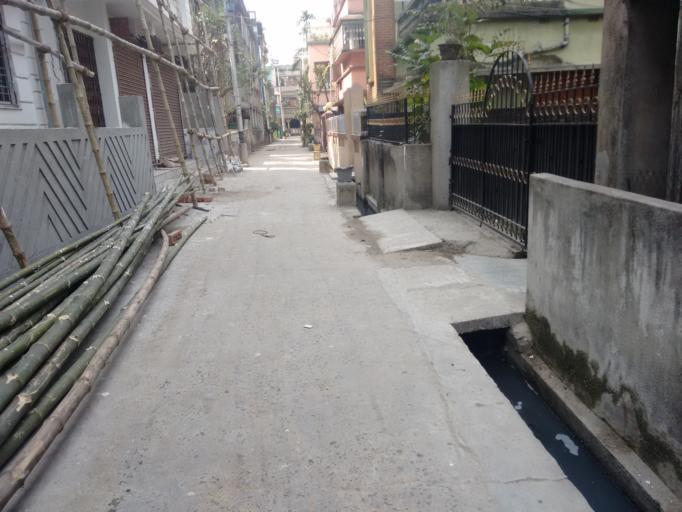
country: IN
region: West Bengal
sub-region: North 24 Parganas
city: Dam Dam
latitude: 22.6497
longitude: 88.4267
